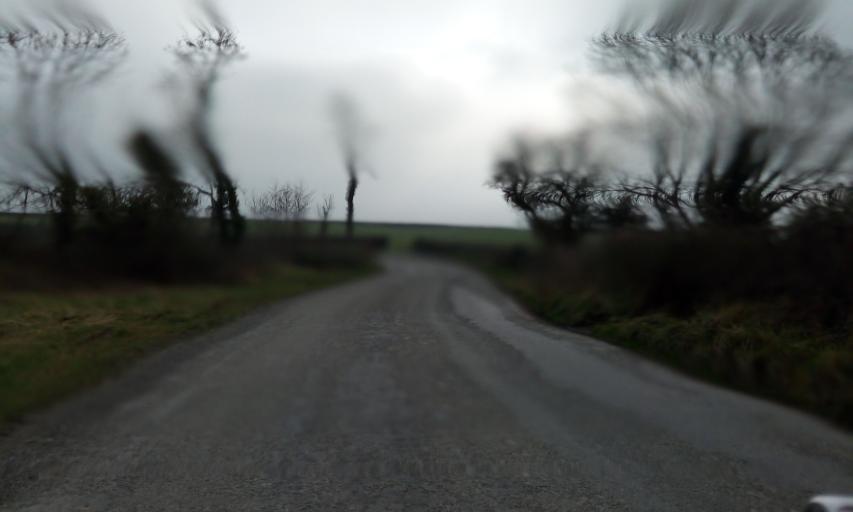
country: IE
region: Leinster
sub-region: Kilkenny
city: Kilkenny
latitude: 52.6579
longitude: -7.1819
